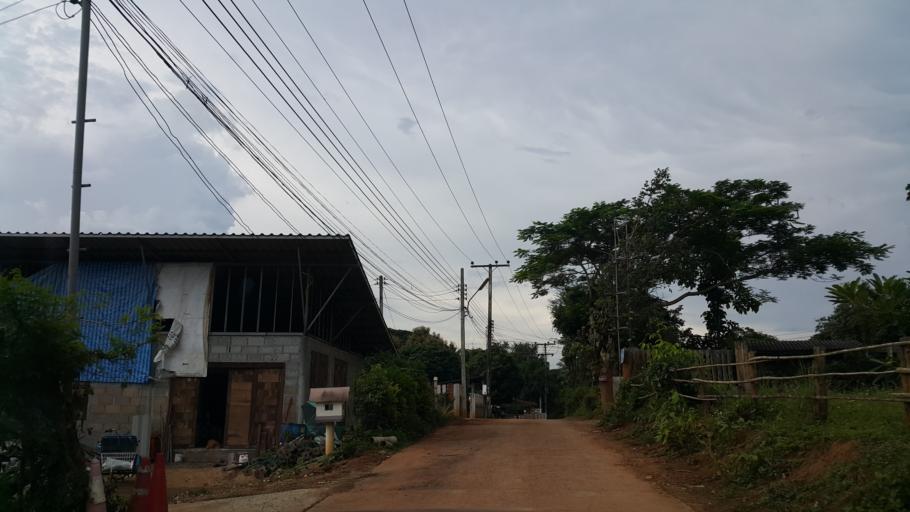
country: TH
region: Chiang Mai
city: Mae On
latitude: 18.9008
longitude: 99.2367
